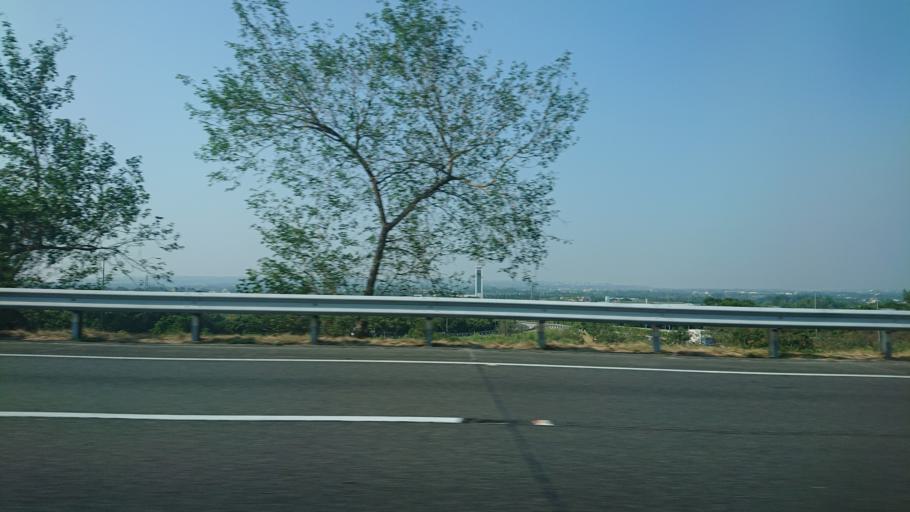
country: TW
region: Taiwan
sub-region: Nantou
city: Nantou
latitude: 23.8515
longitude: 120.7027
